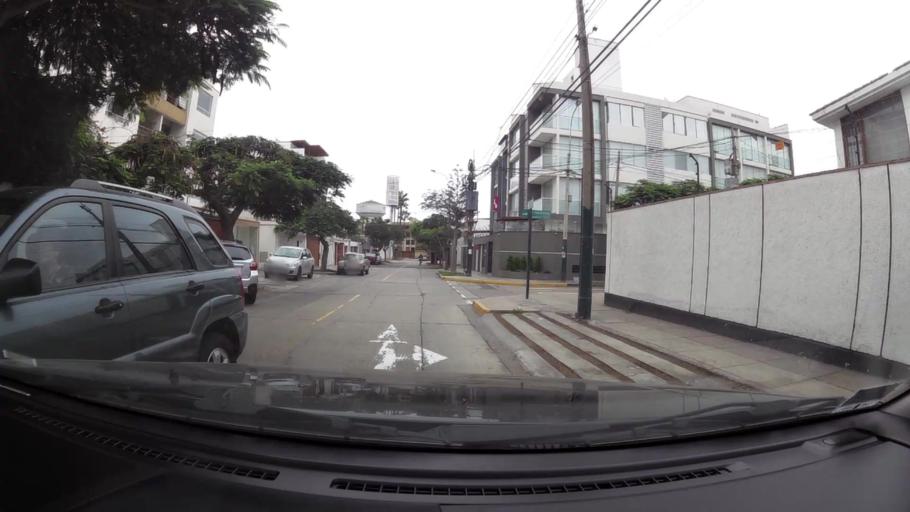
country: PE
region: Lima
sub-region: Lima
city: Surco
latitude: -12.1169
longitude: -76.9926
